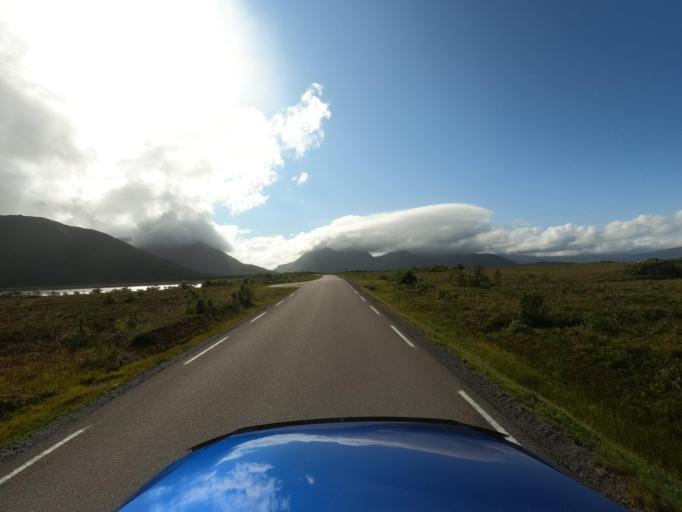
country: NO
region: Nordland
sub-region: Vagan
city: Kabelvag
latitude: 68.3069
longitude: 14.1703
